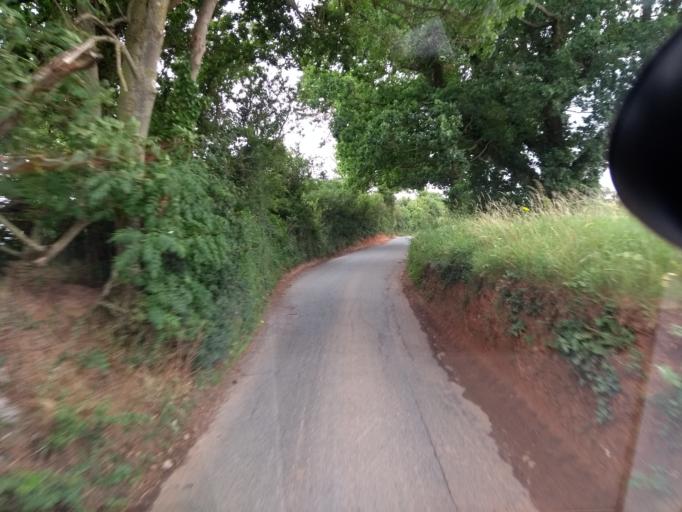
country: GB
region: England
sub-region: Somerset
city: Bridgwater
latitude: 51.1304
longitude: -3.0424
